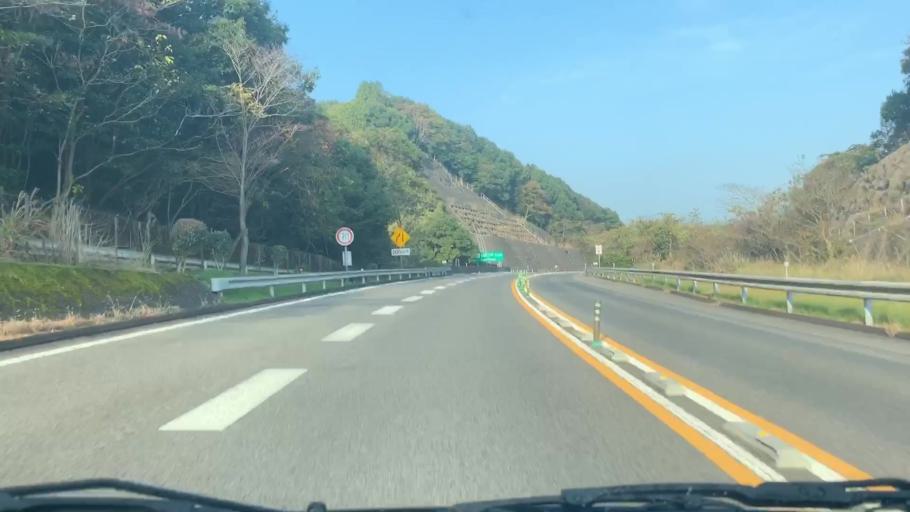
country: JP
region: Saga Prefecture
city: Imaricho-ko
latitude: 33.1600
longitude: 129.8668
